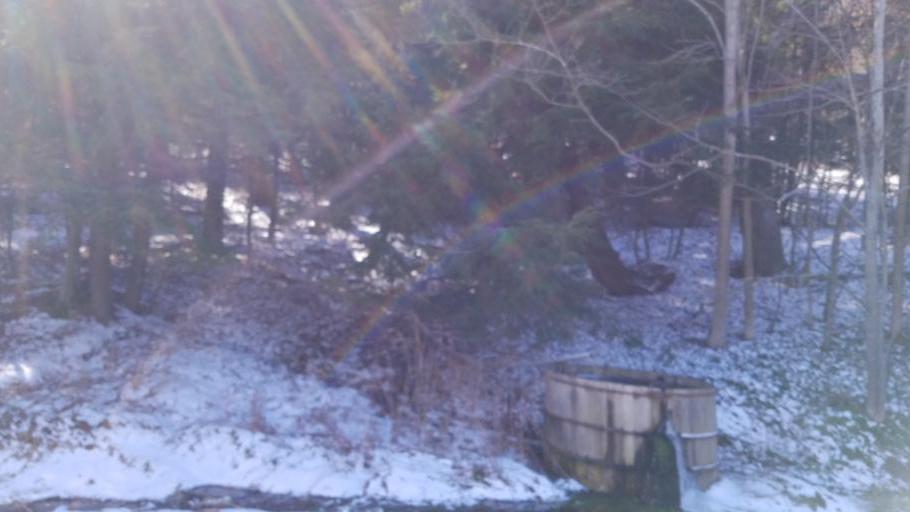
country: US
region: New York
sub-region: Allegany County
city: Wellsville
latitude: 41.9637
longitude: -77.8460
